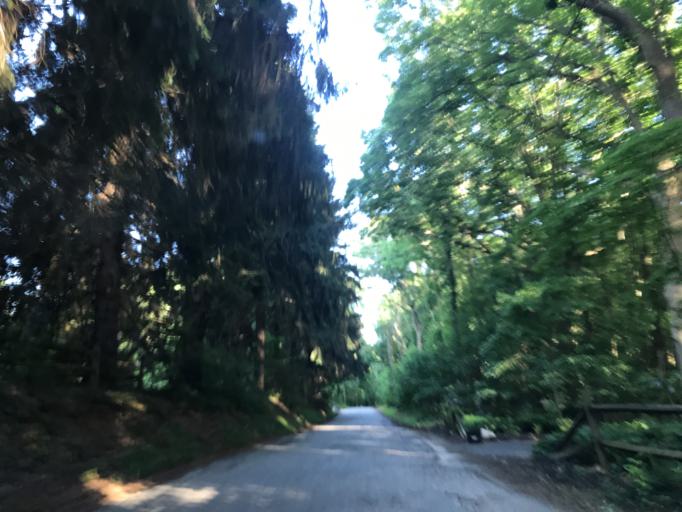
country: US
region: Maryland
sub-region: Harford County
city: Fallston
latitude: 39.5000
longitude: -76.4909
